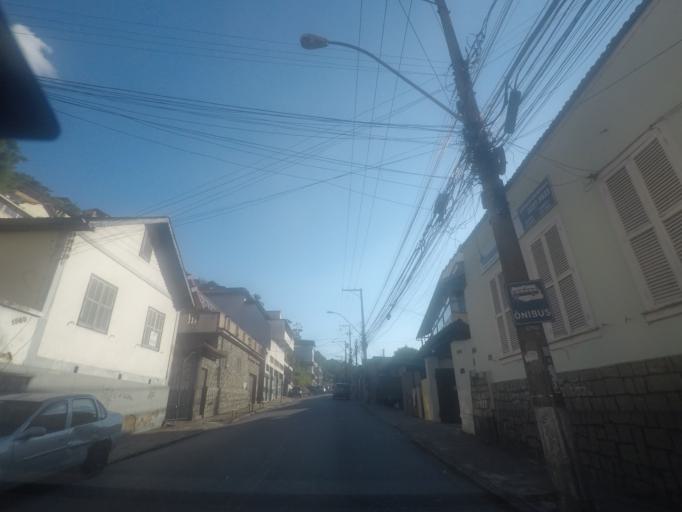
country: BR
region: Rio de Janeiro
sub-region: Petropolis
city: Petropolis
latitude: -22.4923
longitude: -43.1574
